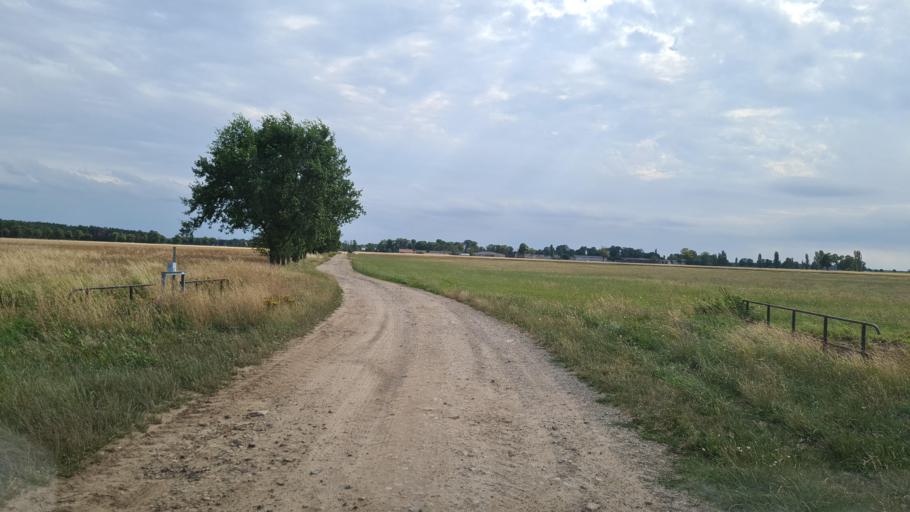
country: DE
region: Saxony-Anhalt
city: Holzdorf
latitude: 51.8080
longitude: 13.1818
